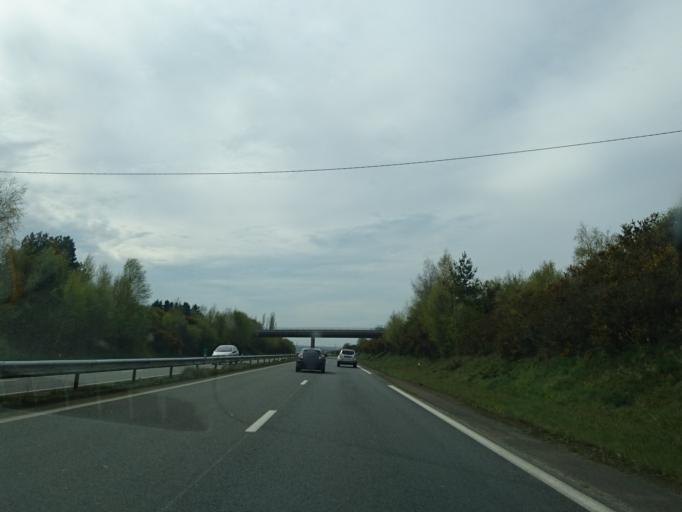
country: FR
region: Brittany
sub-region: Departement des Cotes-d'Armor
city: Jugon-les-Lacs
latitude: 48.4172
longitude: -2.2936
